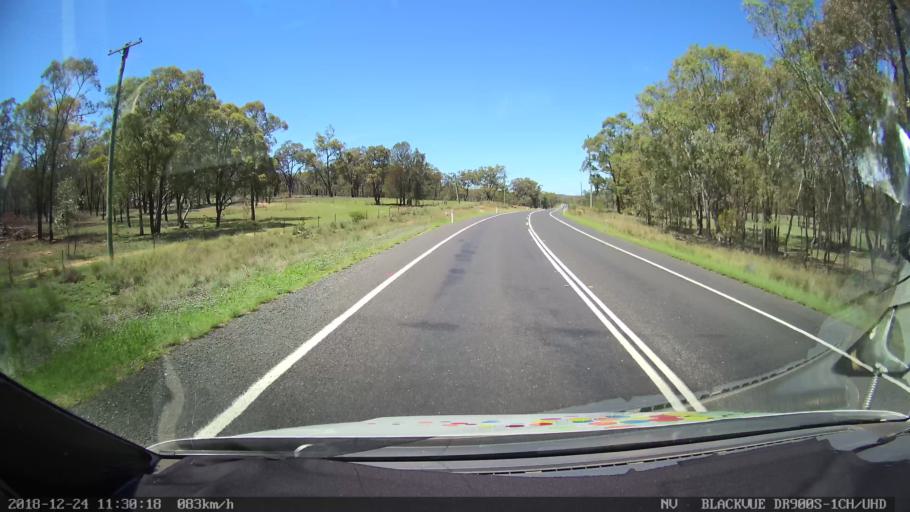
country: AU
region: New South Wales
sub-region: Upper Hunter Shire
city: Merriwa
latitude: -32.2032
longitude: 150.4673
